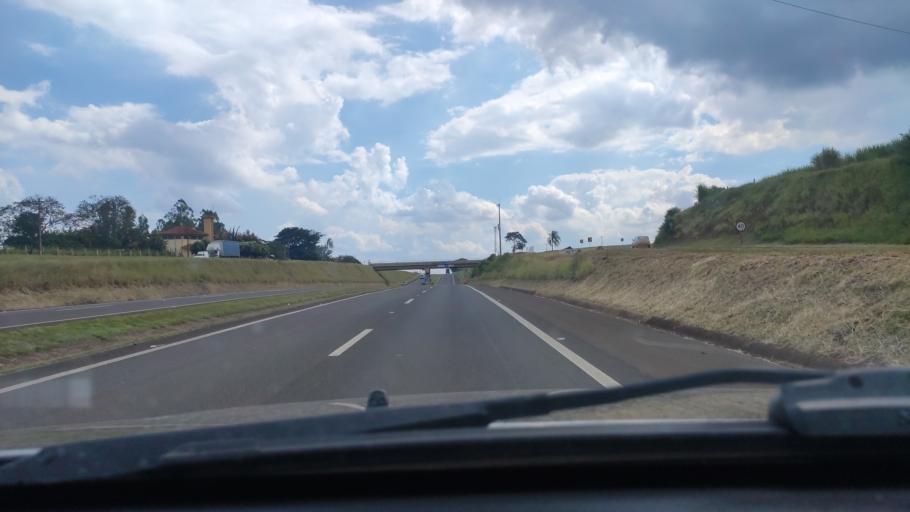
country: BR
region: Sao Paulo
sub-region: Itapui
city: Itapui
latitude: -22.3092
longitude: -48.6894
